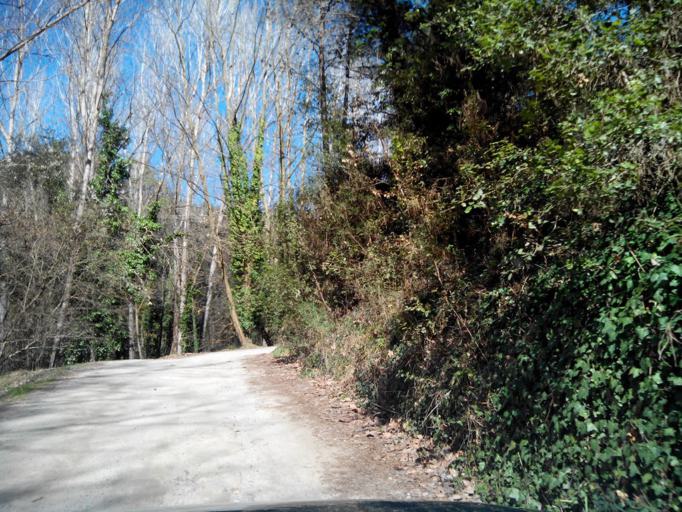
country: ES
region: Catalonia
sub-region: Provincia de Barcelona
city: Dosrius
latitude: 41.6032
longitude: 2.4530
